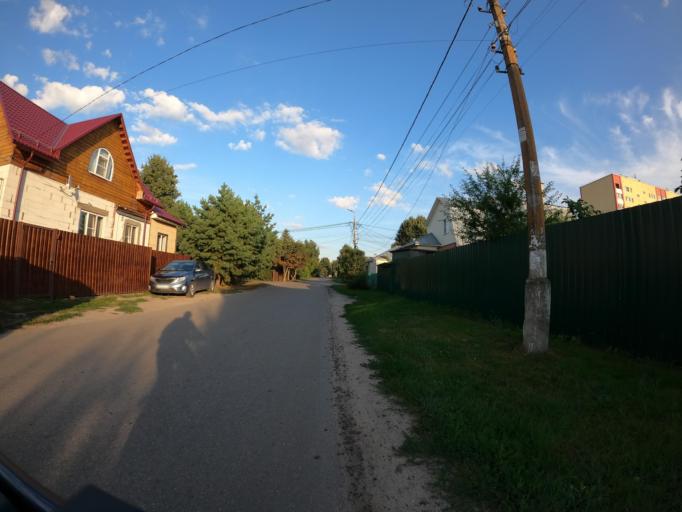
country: RU
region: Moskovskaya
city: Raduzhnyy
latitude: 55.1088
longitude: 38.7456
